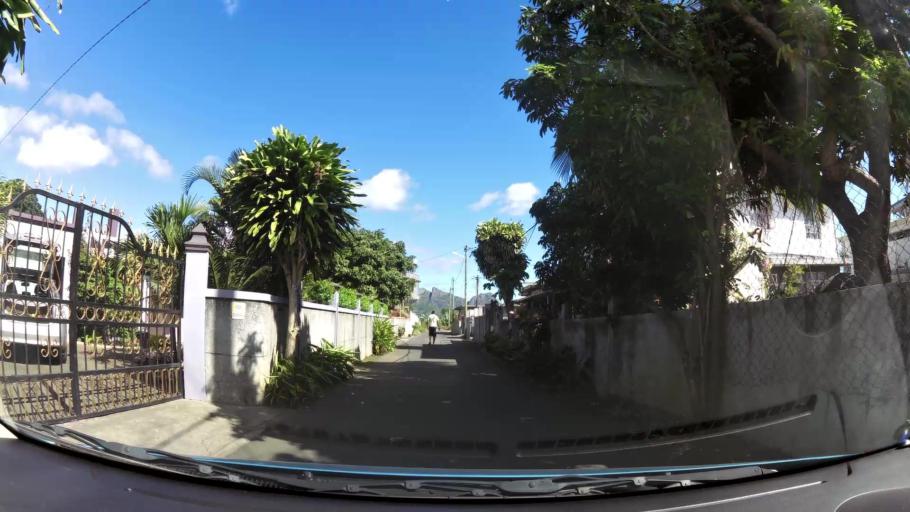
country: MU
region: Plaines Wilhems
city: Vacoas
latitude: -20.2815
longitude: 57.4724
